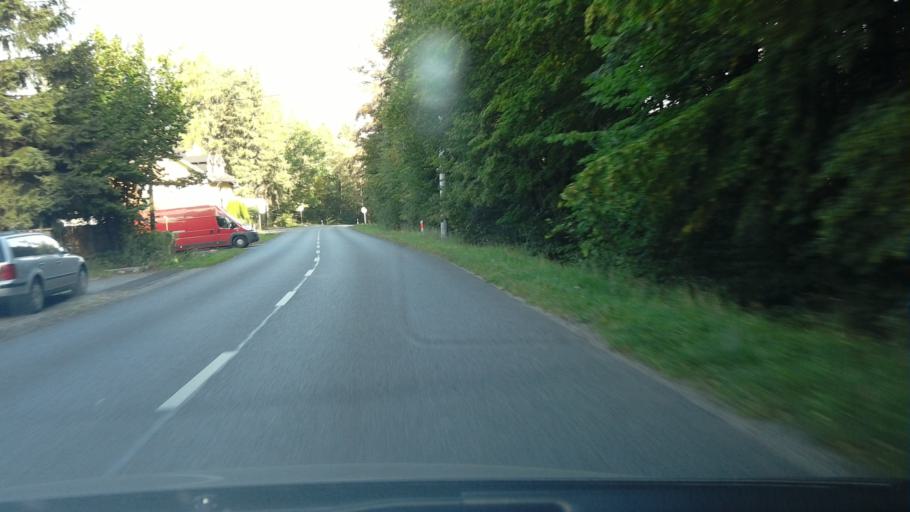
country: PL
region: Lower Silesian Voivodeship
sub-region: Powiat jeleniogorski
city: Karpacz
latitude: 50.7943
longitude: 15.7628
